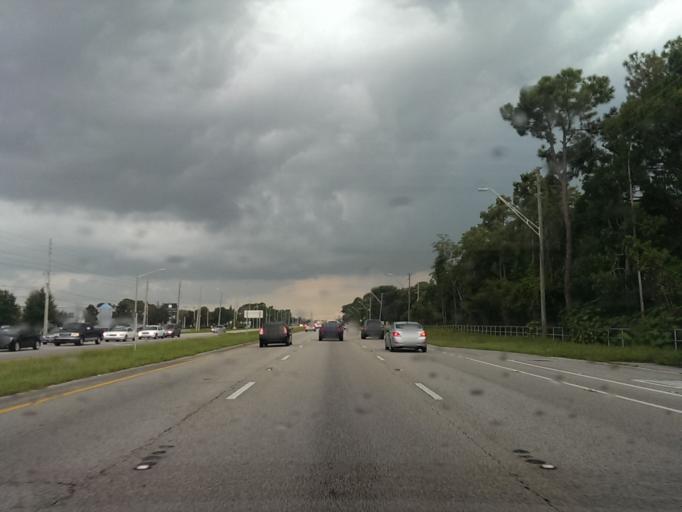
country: US
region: Florida
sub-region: Orange County
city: Orlovista
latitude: 28.5039
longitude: -81.4591
